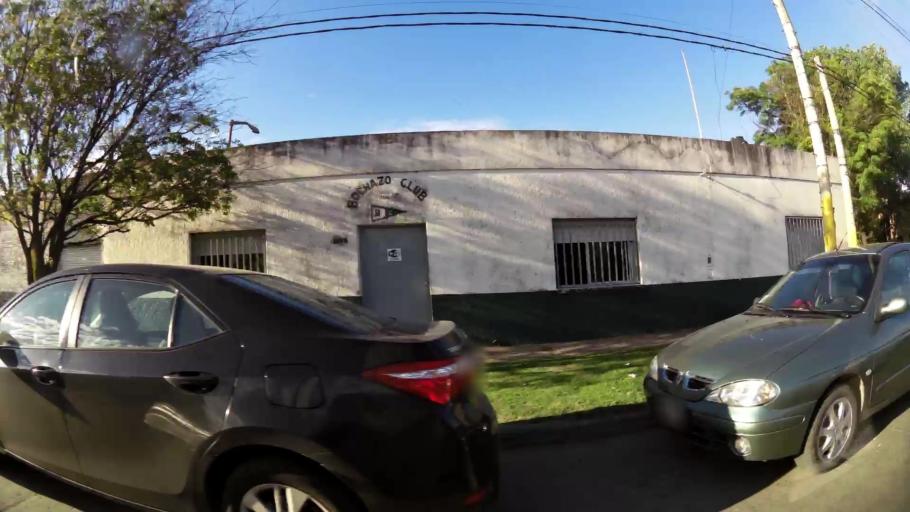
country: AR
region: Santa Fe
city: Gobernador Galvez
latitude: -32.9915
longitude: -60.6756
